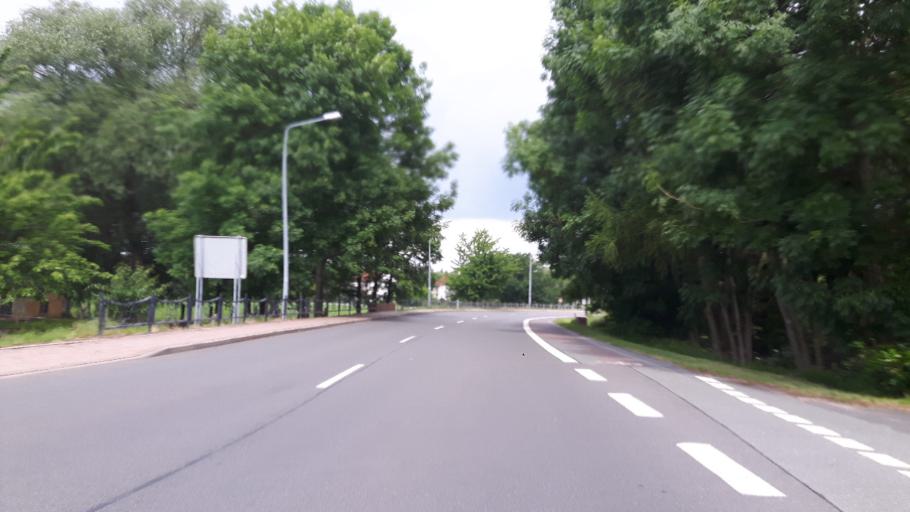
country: DE
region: Saxony-Anhalt
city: Schlaitz
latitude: 51.6714
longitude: 12.4447
